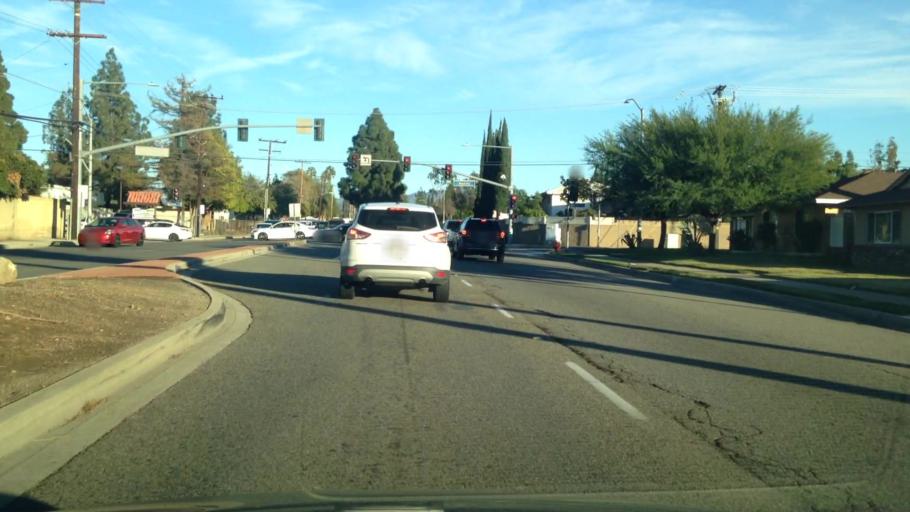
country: US
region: California
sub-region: Orange County
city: Villa Park
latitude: 33.8103
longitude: -117.8278
